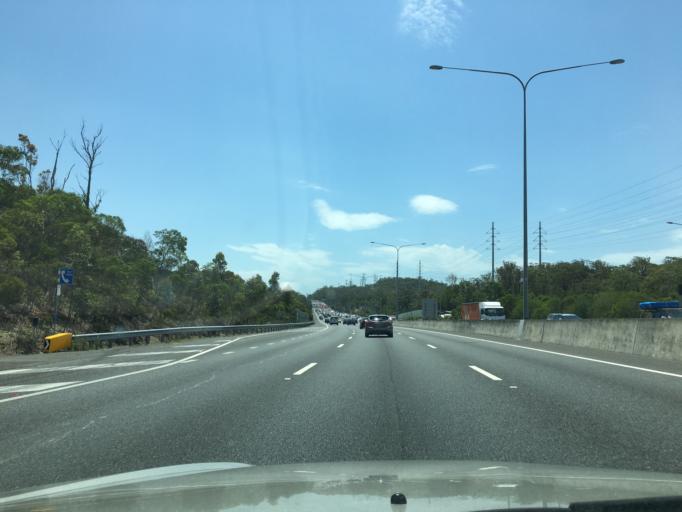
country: AU
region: Queensland
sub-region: Brisbane
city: Mackenzie
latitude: -27.5322
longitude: 153.1227
